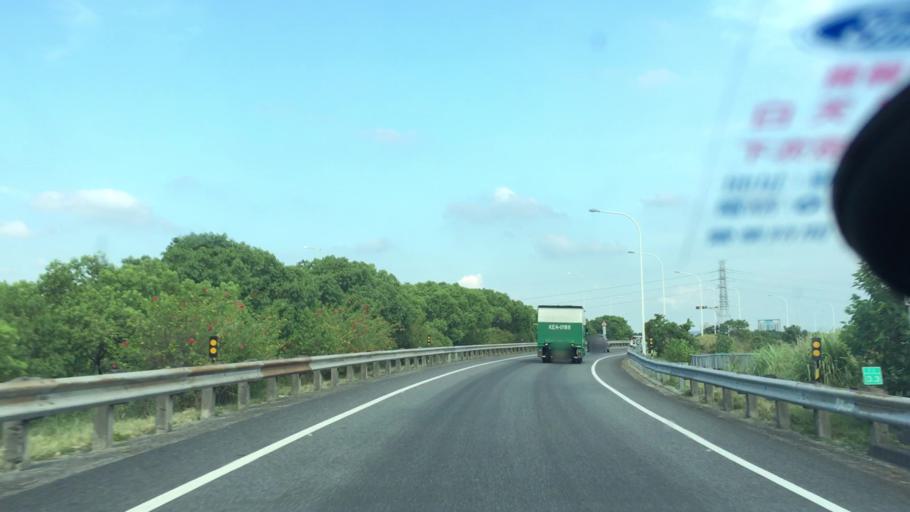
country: TW
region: Taiwan
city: Taoyuan City
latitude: 25.0164
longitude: 121.2739
